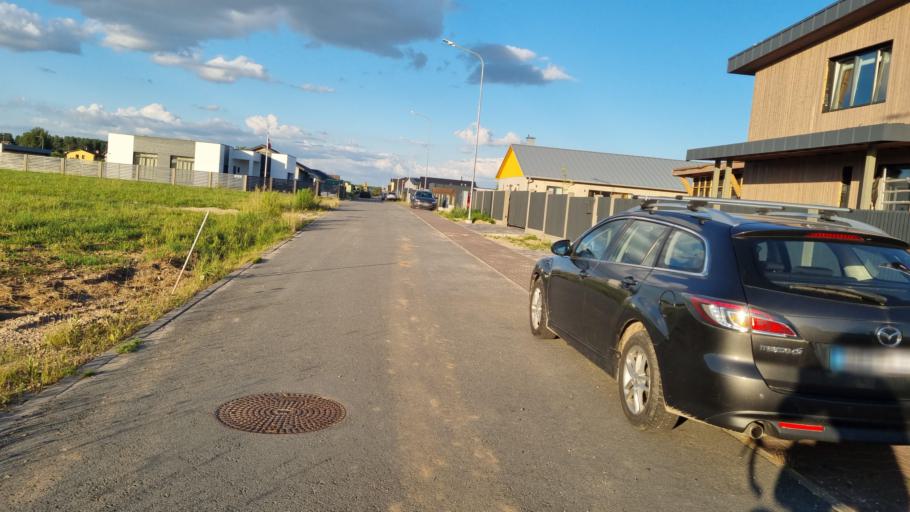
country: LV
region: Kekava
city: Balozi
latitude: 56.8920
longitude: 24.1645
